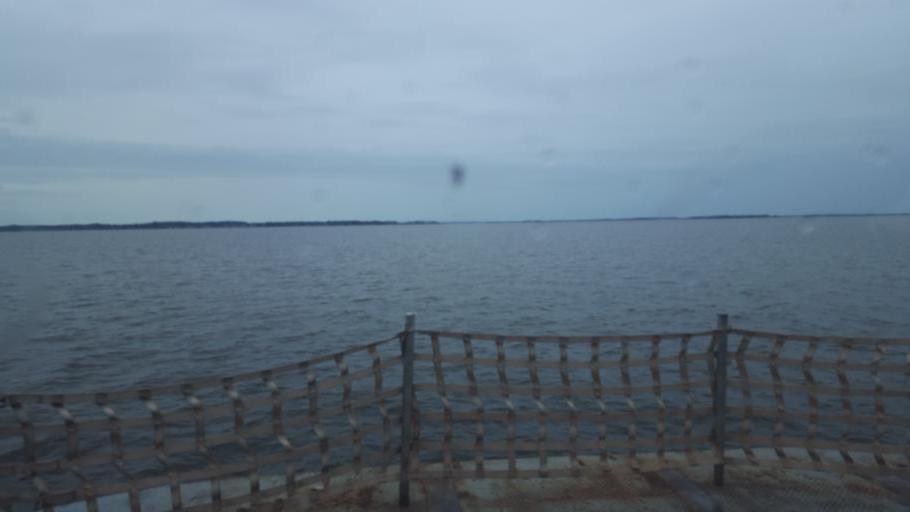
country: US
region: North Carolina
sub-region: Currituck County
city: Currituck
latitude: 36.4690
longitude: -75.9568
